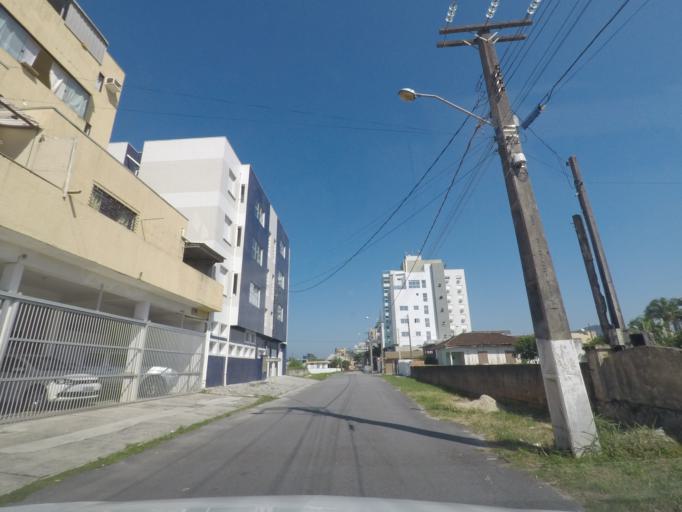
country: BR
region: Parana
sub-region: Guaratuba
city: Guaratuba
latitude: -25.8204
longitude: -48.5315
